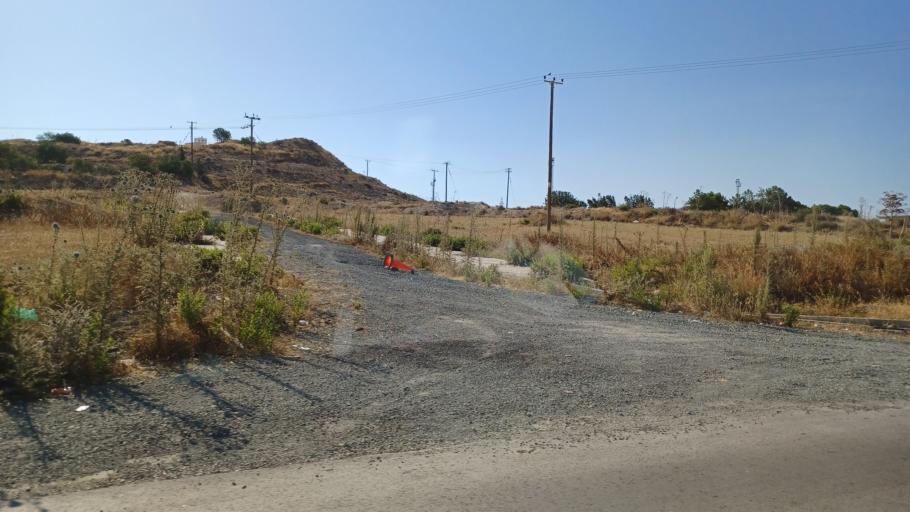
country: CY
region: Larnaka
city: Pyla
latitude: 35.0002
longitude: 33.6922
